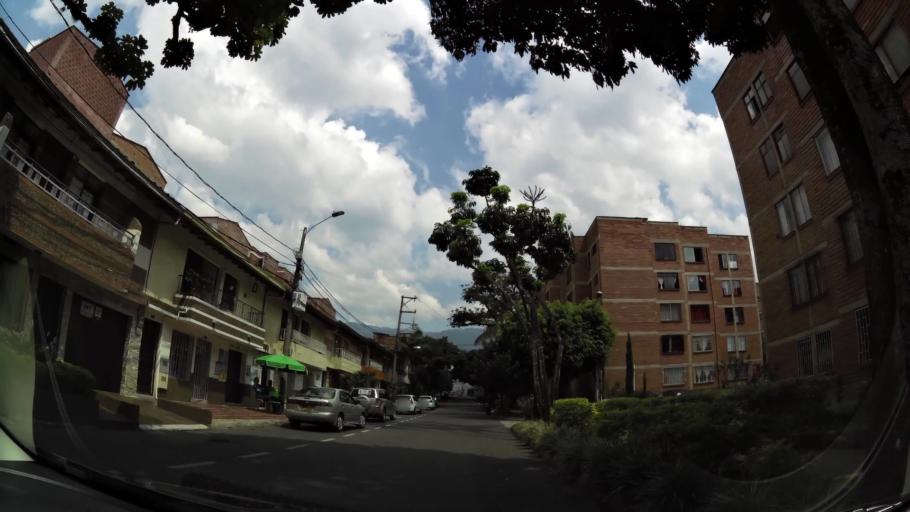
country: CO
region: Antioquia
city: Envigado
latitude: 6.1687
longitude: -75.5945
